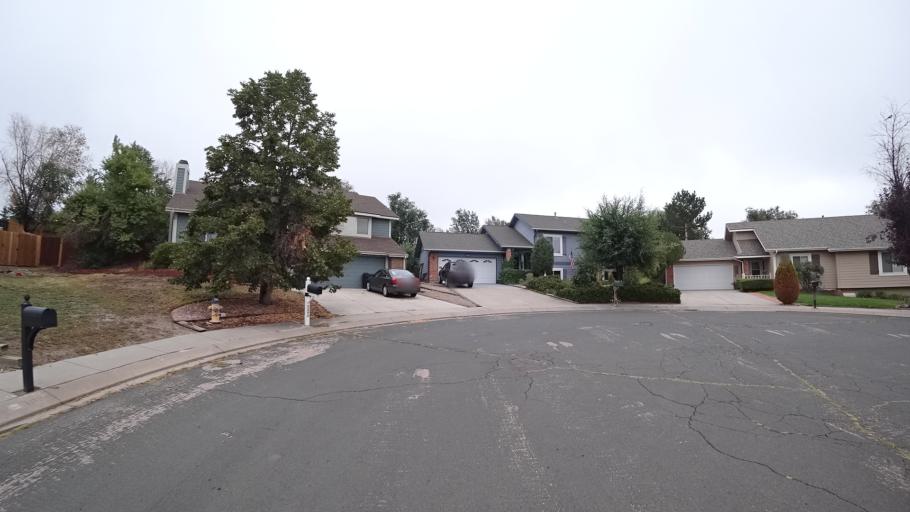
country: US
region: Colorado
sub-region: El Paso County
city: Cimarron Hills
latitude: 38.9328
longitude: -104.7699
